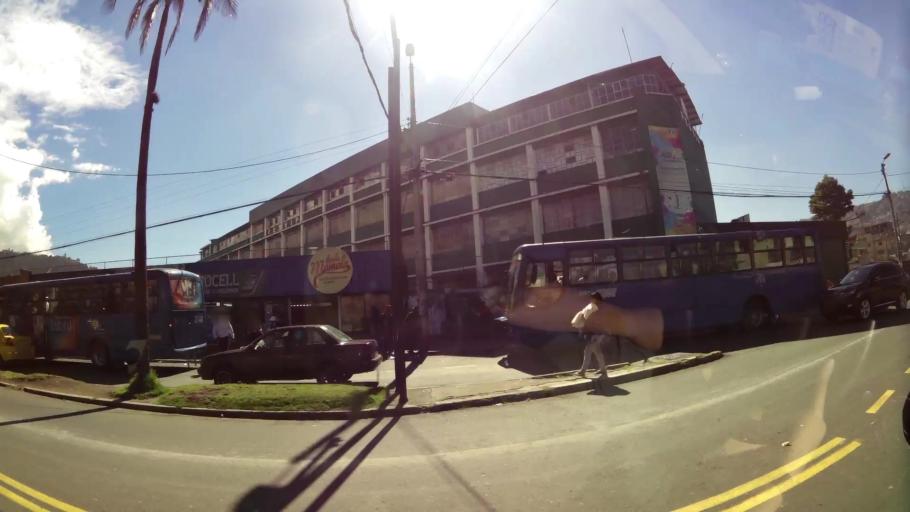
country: EC
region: Pichincha
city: Quito
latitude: -0.2439
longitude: -78.5194
